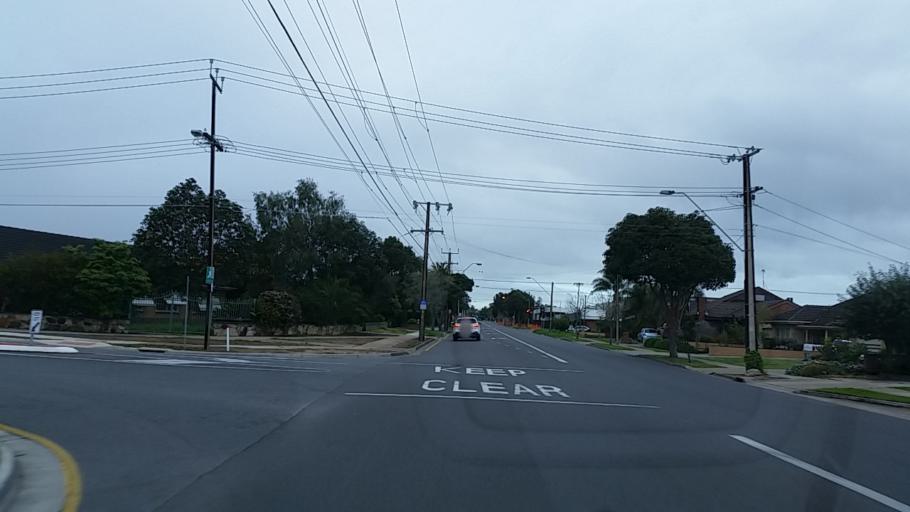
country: AU
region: South Australia
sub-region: Charles Sturt
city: Findon
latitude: -34.9122
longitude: 138.5339
